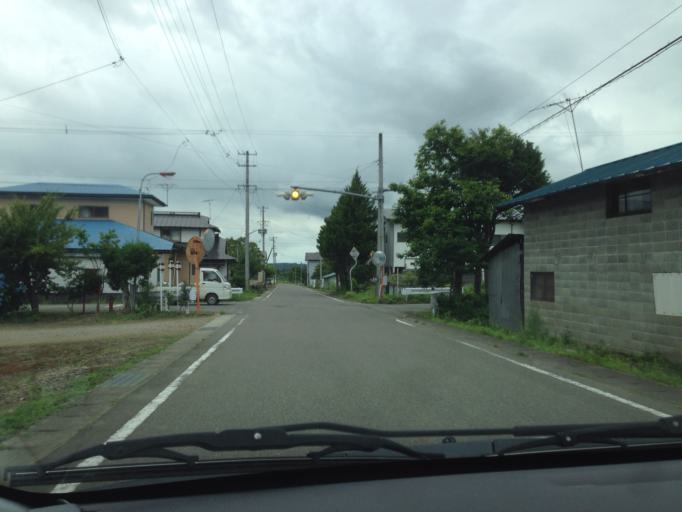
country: JP
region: Fukushima
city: Kitakata
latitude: 37.7124
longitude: 139.8765
